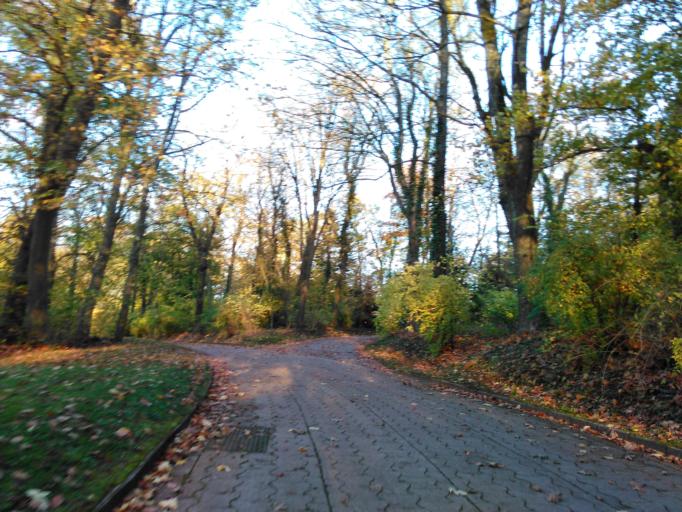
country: LU
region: Luxembourg
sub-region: Canton d'Esch-sur-Alzette
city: Esch-sur-Alzette
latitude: 49.4906
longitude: 5.9849
